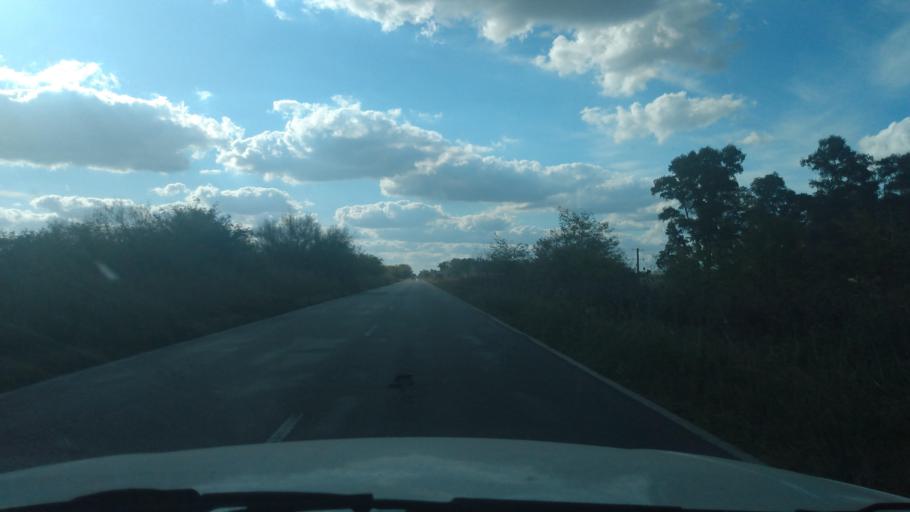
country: AR
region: Buenos Aires
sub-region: Partido de Mercedes
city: Mercedes
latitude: -34.7608
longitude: -59.3759
